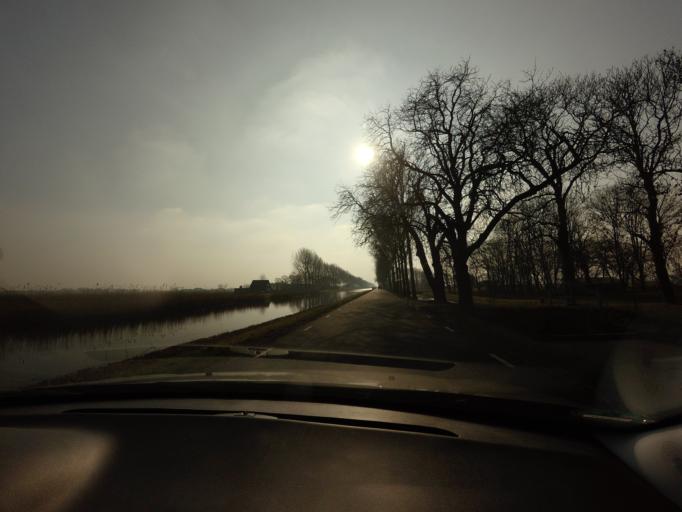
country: NL
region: North Holland
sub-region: Gemeente Alkmaar
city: Alkmaar
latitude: 52.6099
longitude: 4.7933
